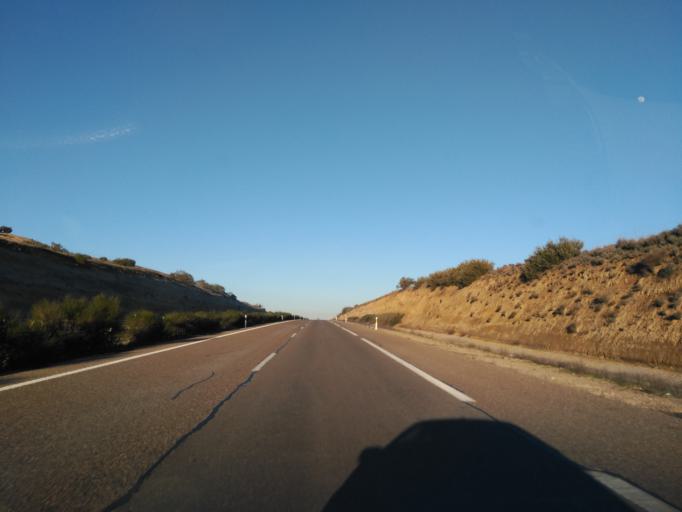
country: ES
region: Castille and Leon
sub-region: Provincia de Zamora
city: Castrillo de la Guarena
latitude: 41.2020
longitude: -5.3365
